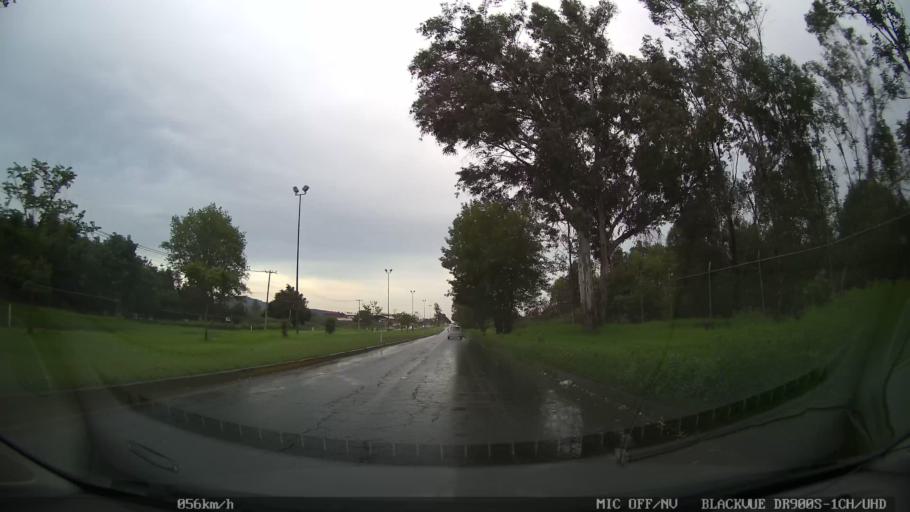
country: MX
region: Michoacan
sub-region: Uruapan
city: Santa Rosa (Santa Barbara)
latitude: 19.3935
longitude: -102.0378
